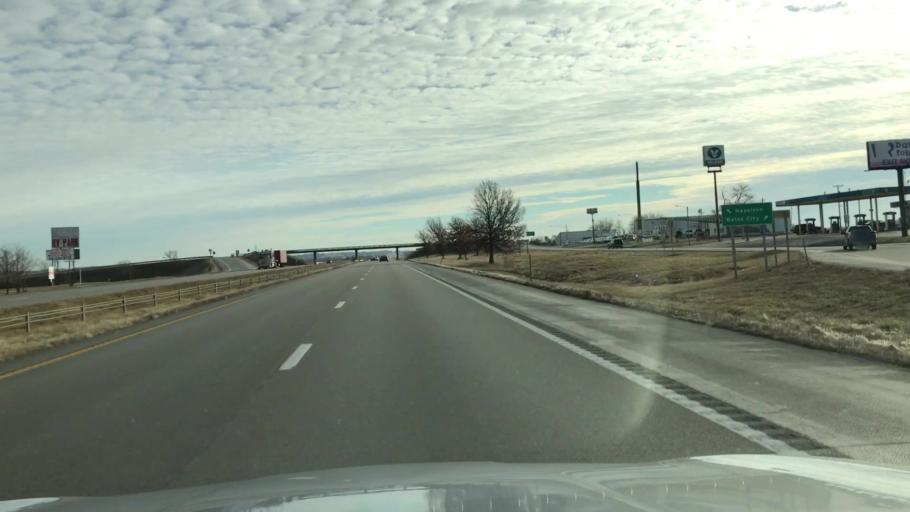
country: US
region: Missouri
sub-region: Jackson County
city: Oak Grove
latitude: 39.0113
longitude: -94.0725
